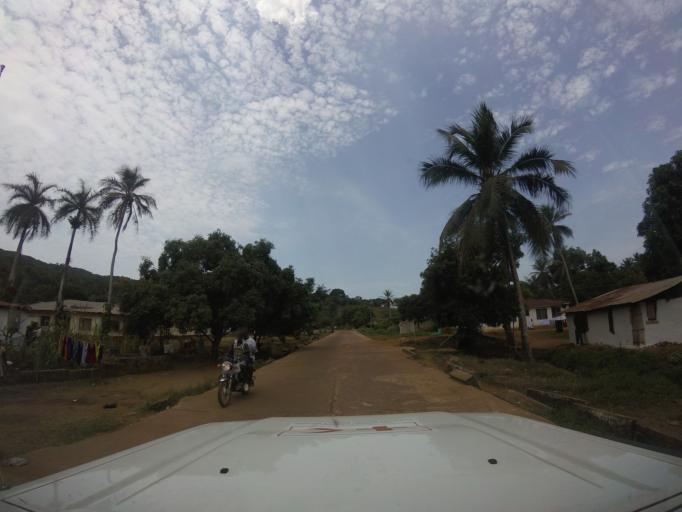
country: LR
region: Grand Cape Mount
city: Robertsport
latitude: 6.7541
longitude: -11.3720
